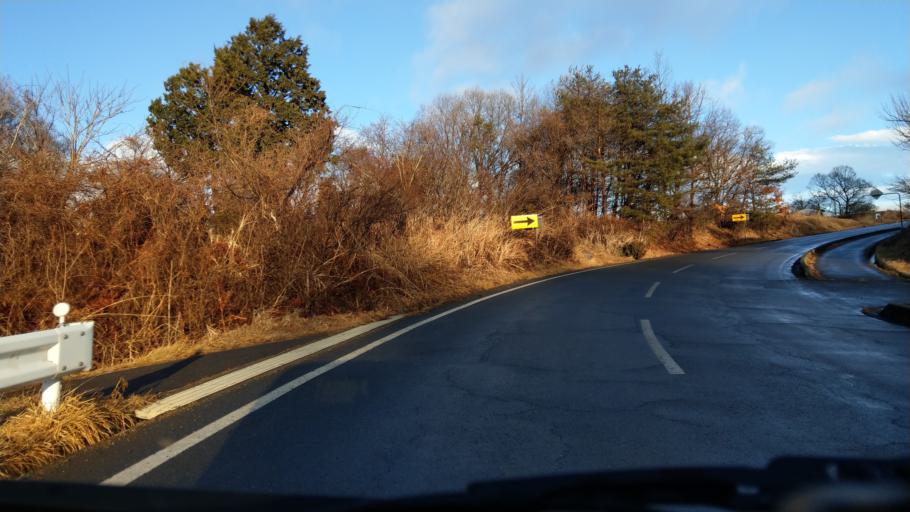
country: JP
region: Nagano
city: Komoro
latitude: 36.3062
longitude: 138.3967
